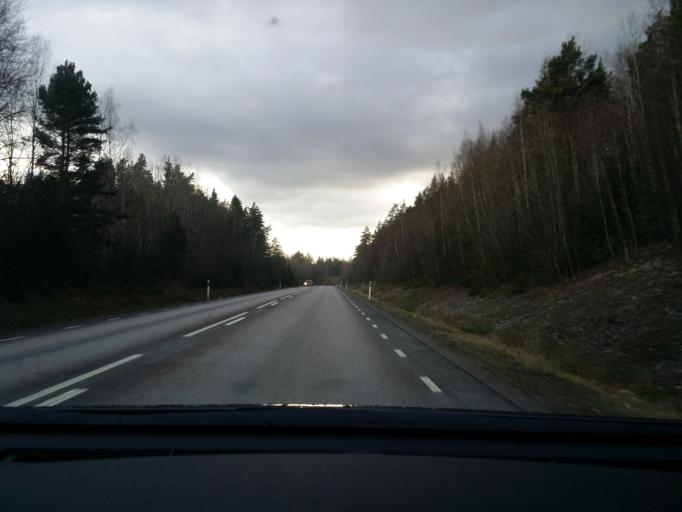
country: SE
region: Soedermanland
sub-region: Eskilstuna Kommun
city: Arla
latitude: 59.3876
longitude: 16.6260
